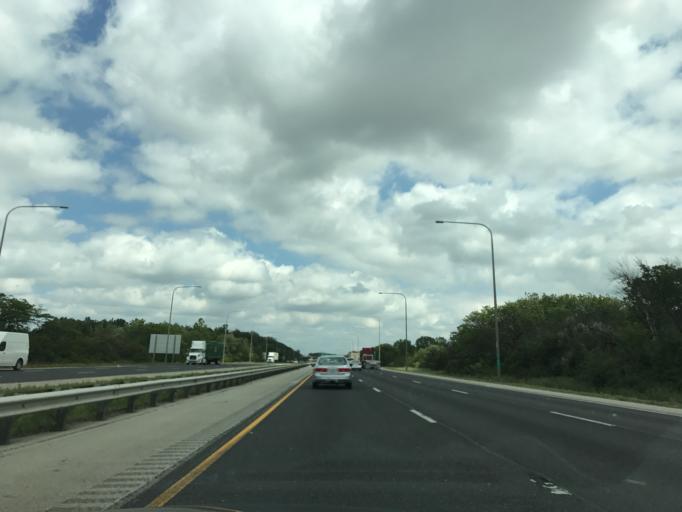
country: US
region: Illinois
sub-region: Cook County
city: Tinley Park
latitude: 41.5578
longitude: -87.7613
